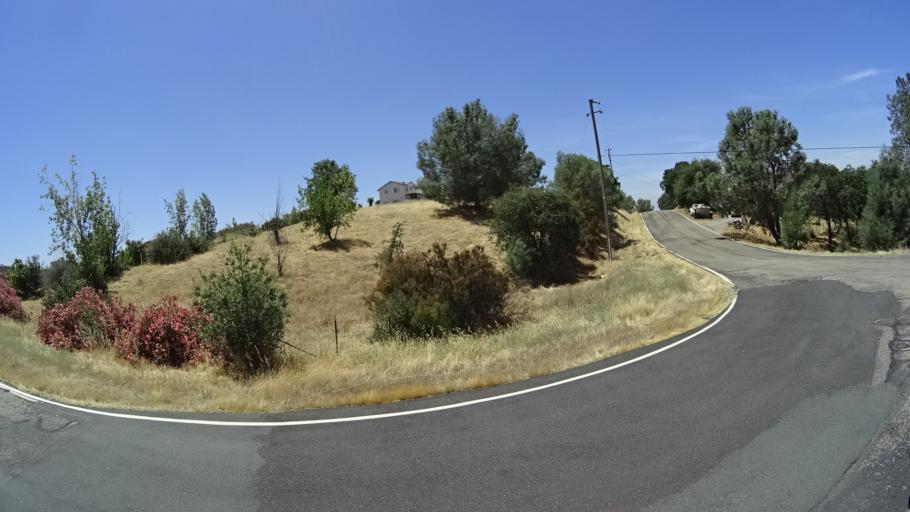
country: US
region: California
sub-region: Calaveras County
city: Rancho Calaveras
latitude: 38.1205
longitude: -120.8427
